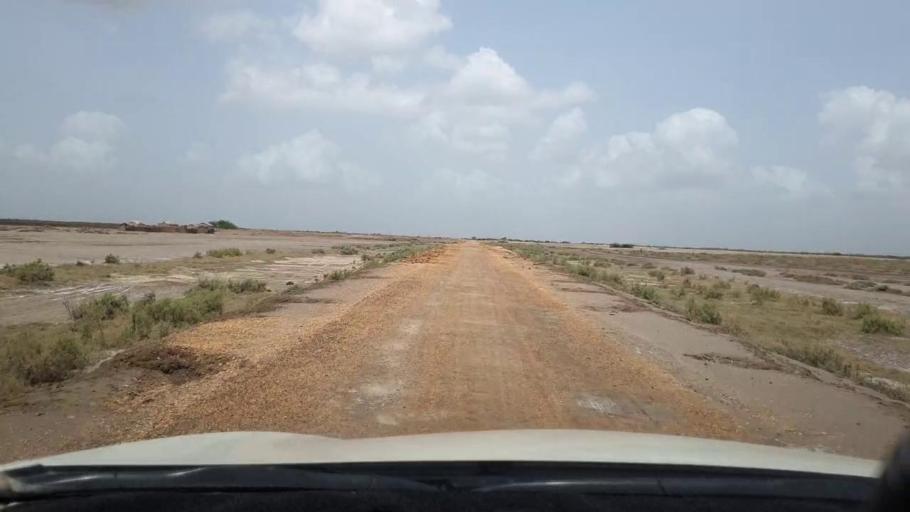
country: PK
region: Sindh
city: Kadhan
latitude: 24.3601
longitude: 68.8275
